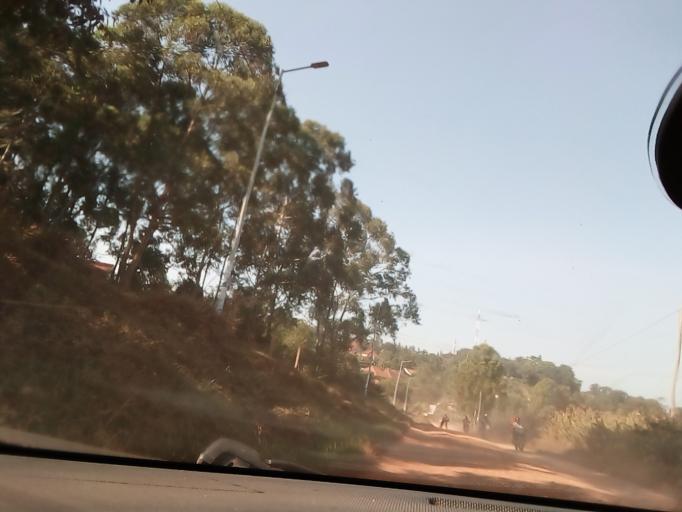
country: UG
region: Central Region
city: Masaka
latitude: -0.3310
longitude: 31.7355
